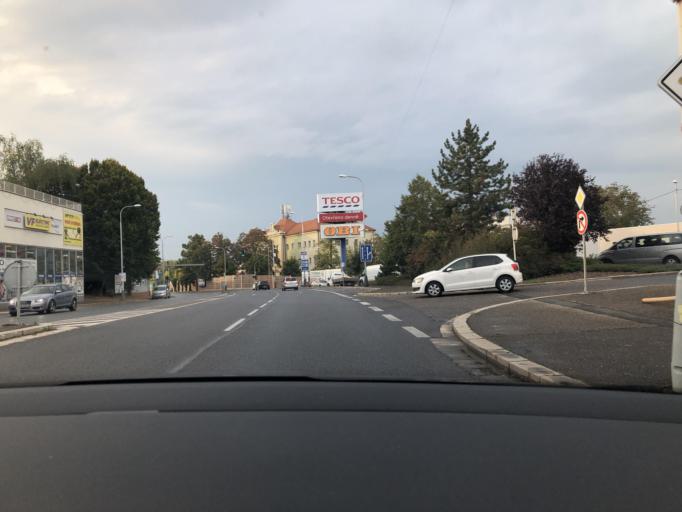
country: CZ
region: Central Bohemia
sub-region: Okres Kolin
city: Kolin
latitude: 50.0299
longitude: 15.1902
